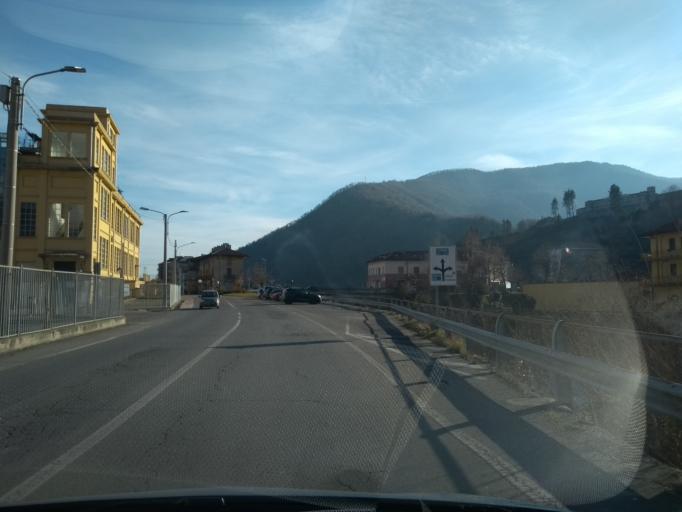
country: IT
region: Piedmont
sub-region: Provincia di Torino
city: Lanzo Torinese
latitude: 45.2749
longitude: 7.4800
